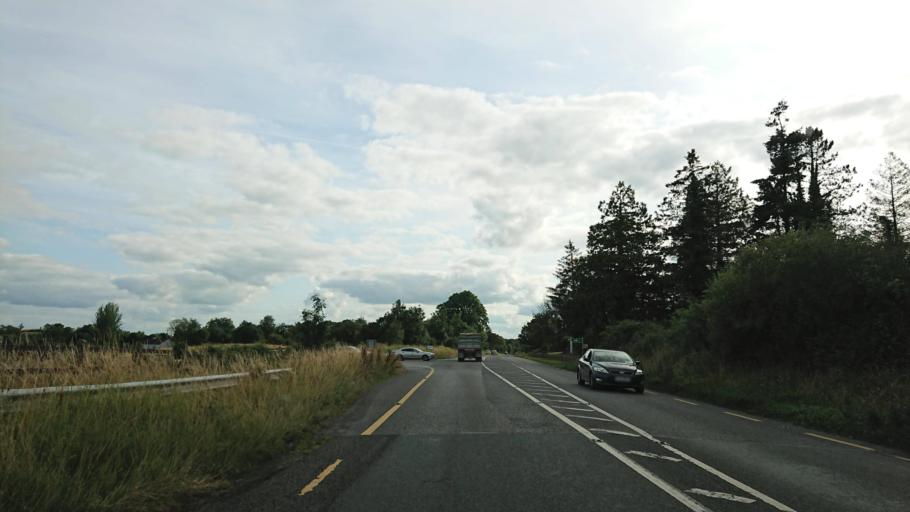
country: IE
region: Connaught
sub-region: County Leitrim
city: Carrick-on-Shannon
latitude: 53.9739
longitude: -8.0617
